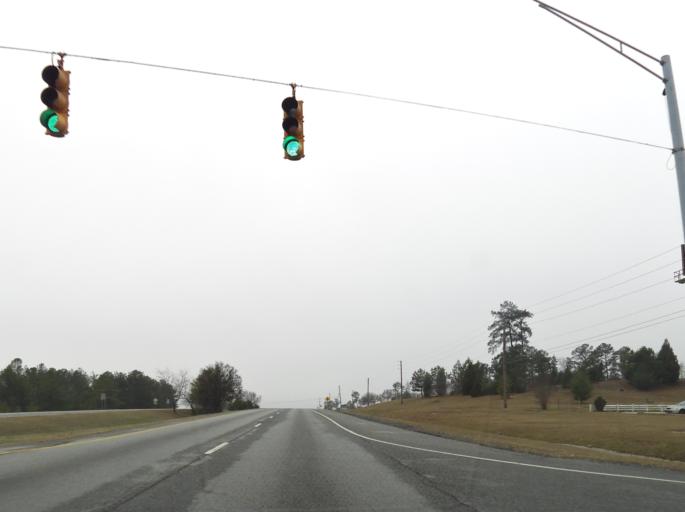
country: US
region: Georgia
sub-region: Bibb County
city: West Point
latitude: 32.8083
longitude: -83.7286
